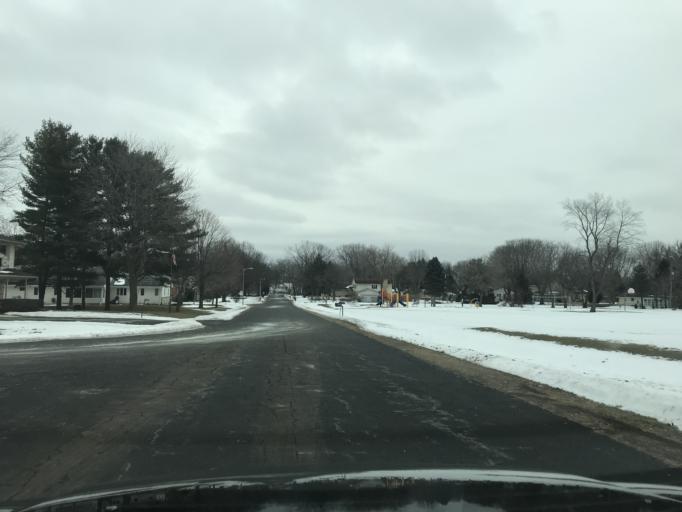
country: US
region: Wisconsin
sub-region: Dane County
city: Monona
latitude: 43.0799
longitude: -89.2713
